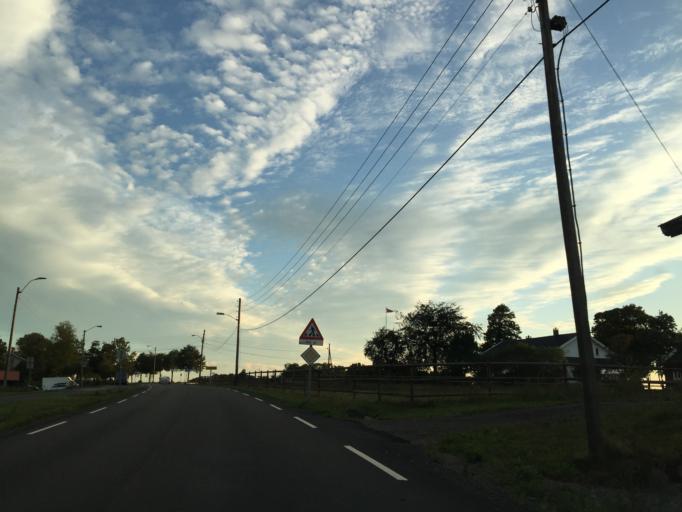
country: NO
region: Akershus
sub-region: As
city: As
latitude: 59.7184
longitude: 10.7781
